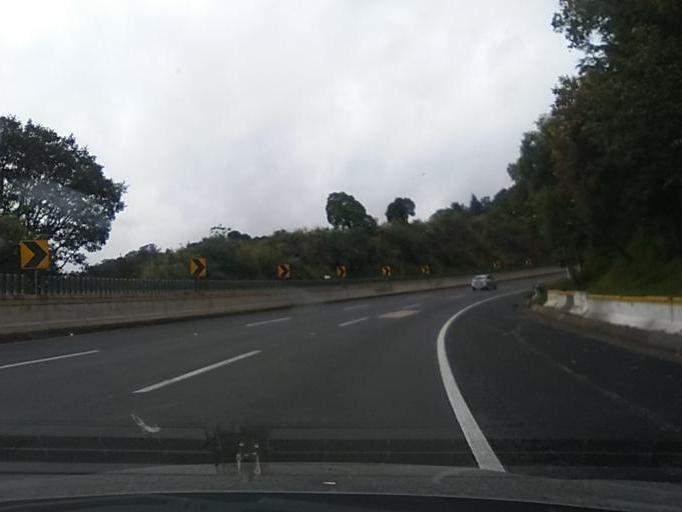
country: MX
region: Mexico City
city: Xochimilco
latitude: 19.2242
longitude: -99.1404
